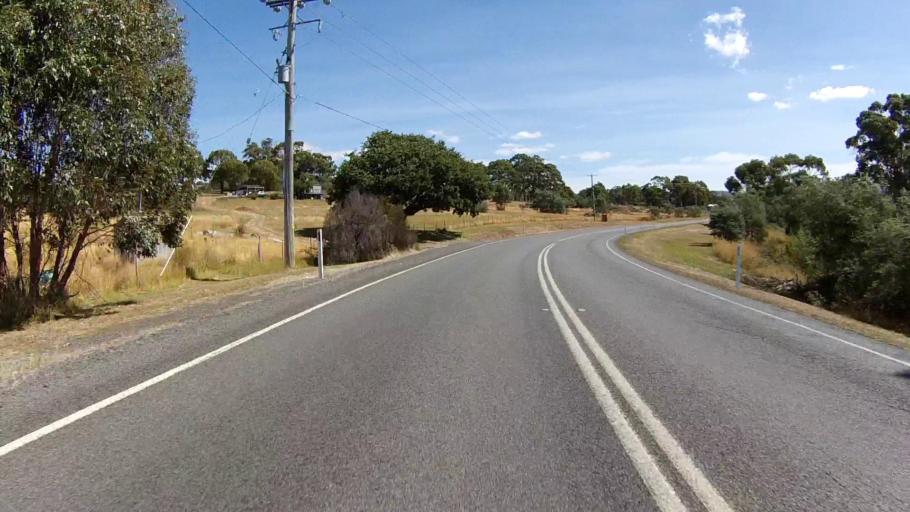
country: AU
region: Tasmania
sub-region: Sorell
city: Sorell
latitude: -42.6104
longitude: 147.7342
